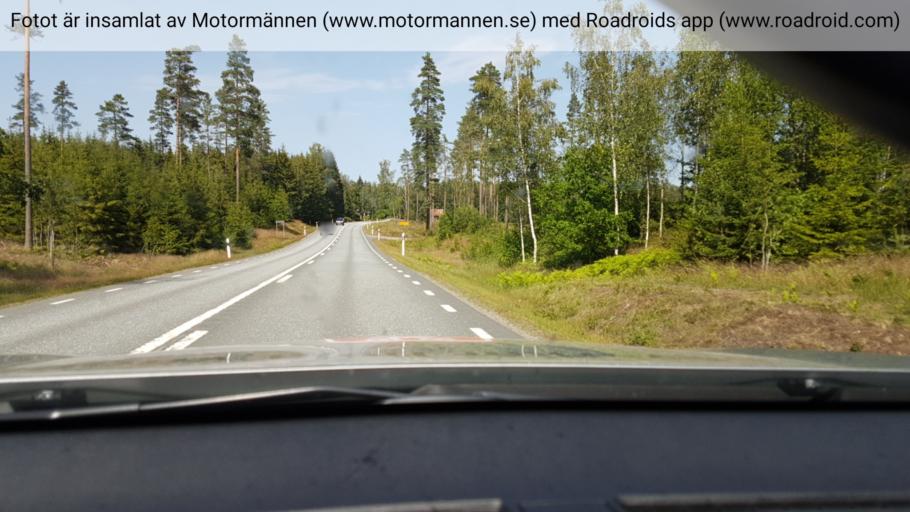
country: SE
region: Joenkoeping
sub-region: Nassjo Kommun
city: Bodafors
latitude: 57.5349
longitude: 14.7873
